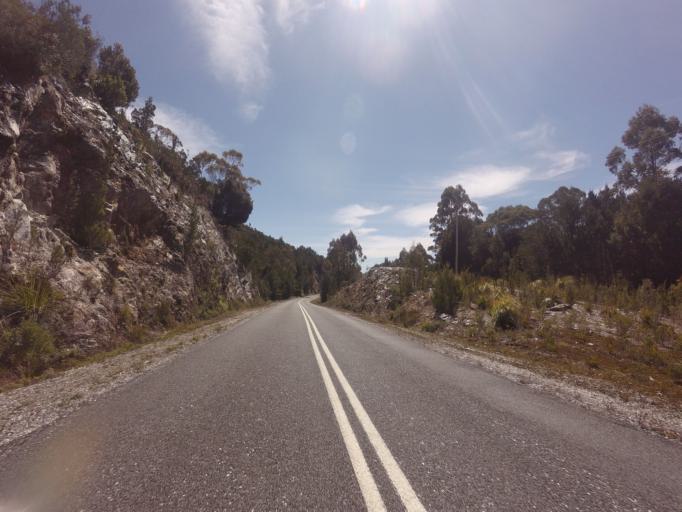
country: AU
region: Tasmania
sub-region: West Coast
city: Queenstown
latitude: -42.7600
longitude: 146.0039
